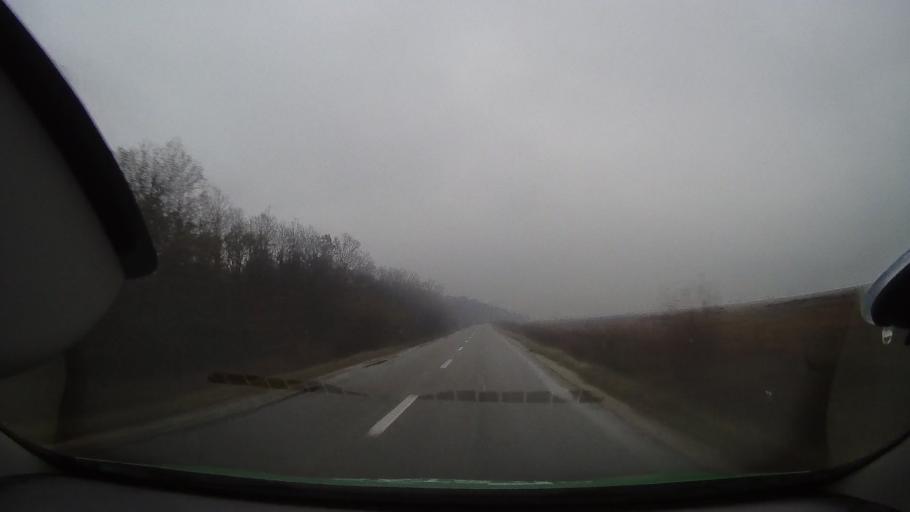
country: RO
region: Bihor
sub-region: Comuna Tinca
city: Gurbediu
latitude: 46.7812
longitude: 21.8706
